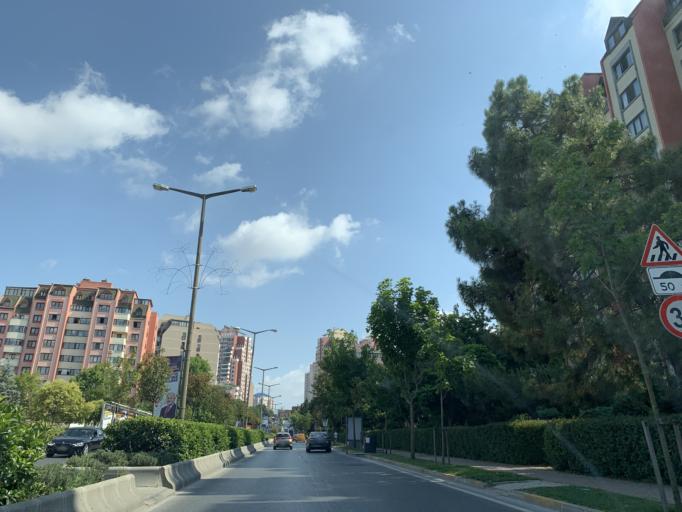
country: TR
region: Istanbul
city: Esenyurt
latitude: 41.0683
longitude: 28.6841
